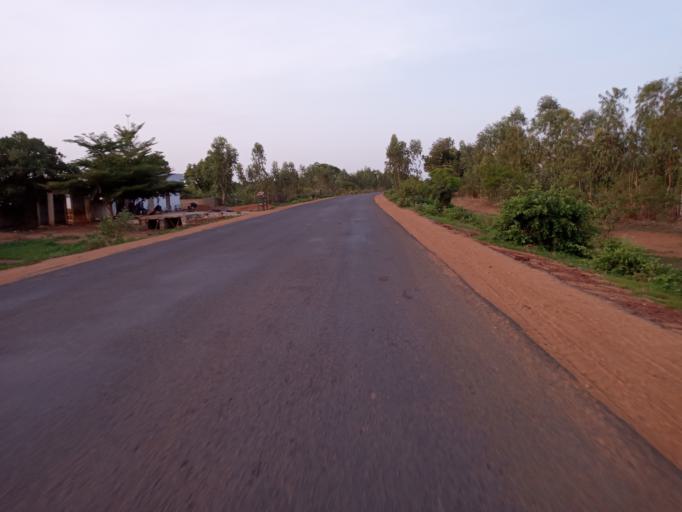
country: ML
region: Bamako
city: Bamako
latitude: 12.2957
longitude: -8.1642
